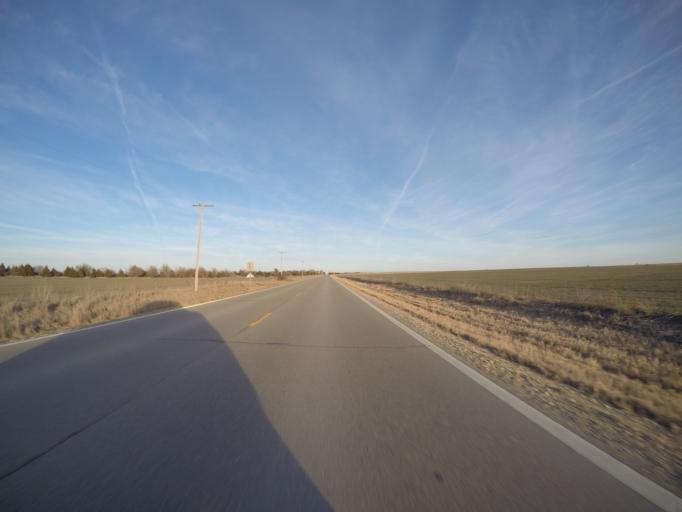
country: US
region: Kansas
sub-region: Dickinson County
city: Herington
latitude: 38.6673
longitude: -96.8923
